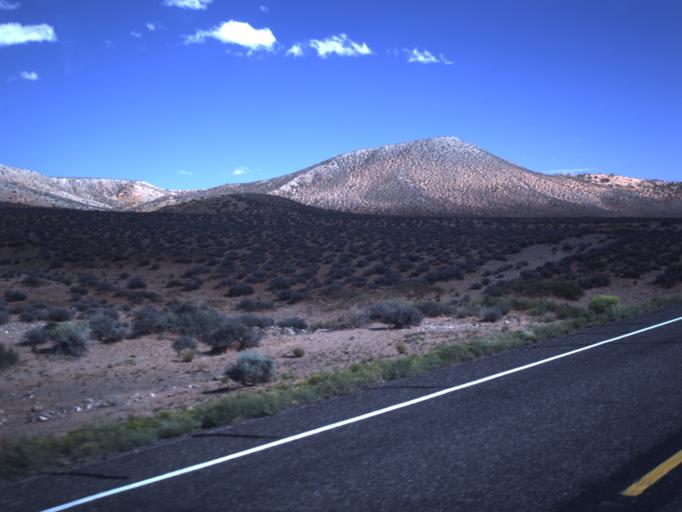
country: US
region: Utah
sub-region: Wayne County
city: Loa
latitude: 38.0818
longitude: -110.6130
